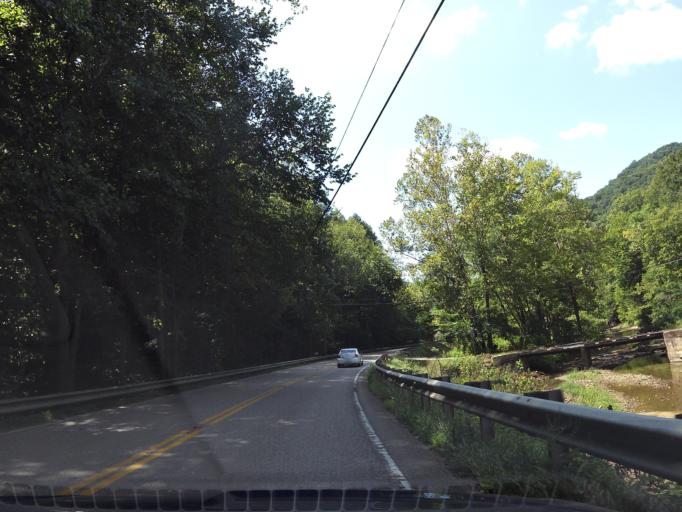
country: US
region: Kentucky
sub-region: Harlan County
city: Loyall
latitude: 36.9598
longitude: -83.3939
